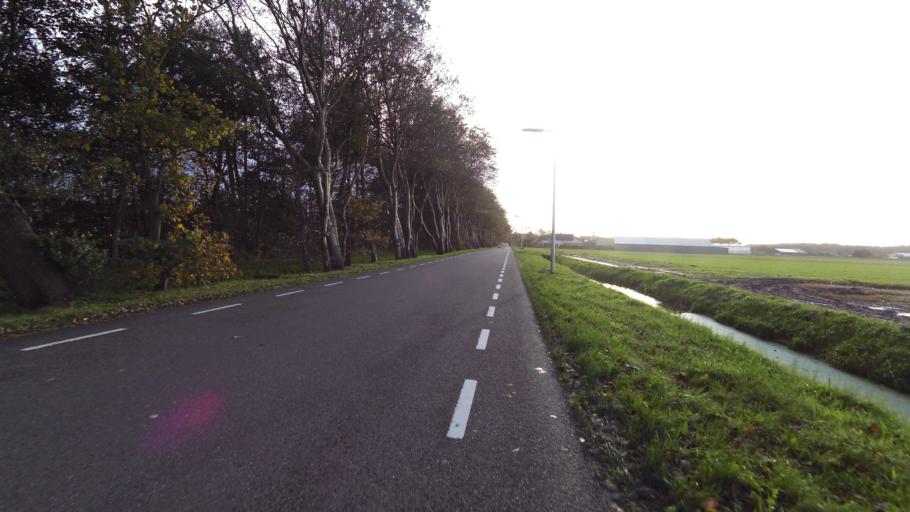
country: NL
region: South Holland
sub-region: Gemeente Noordwijkerhout
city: Noordwijkerhout
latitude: 52.2826
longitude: 4.5007
